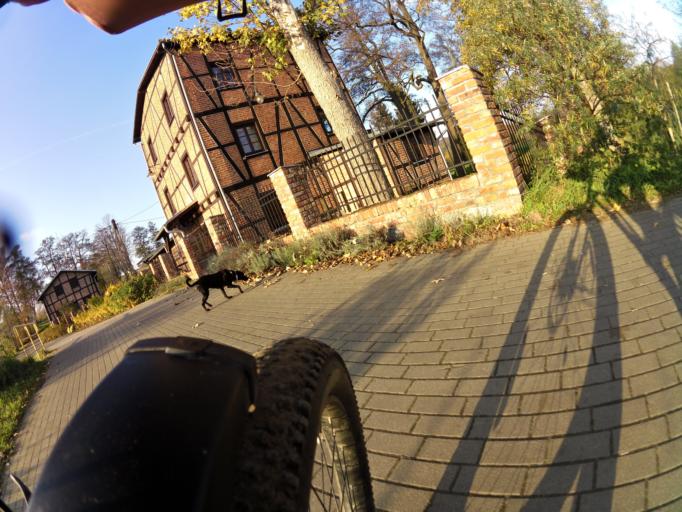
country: PL
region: Pomeranian Voivodeship
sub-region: Powiat pucki
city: Krokowa
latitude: 54.7502
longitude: 18.1903
